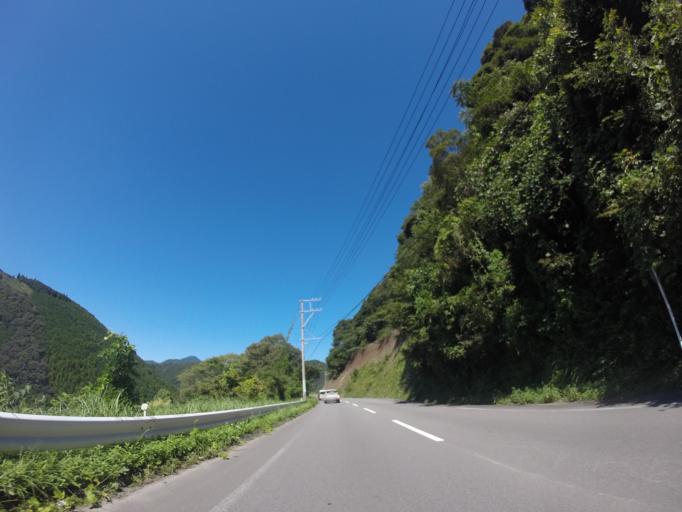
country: JP
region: Shizuoka
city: Kanaya
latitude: 34.8939
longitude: 138.1165
